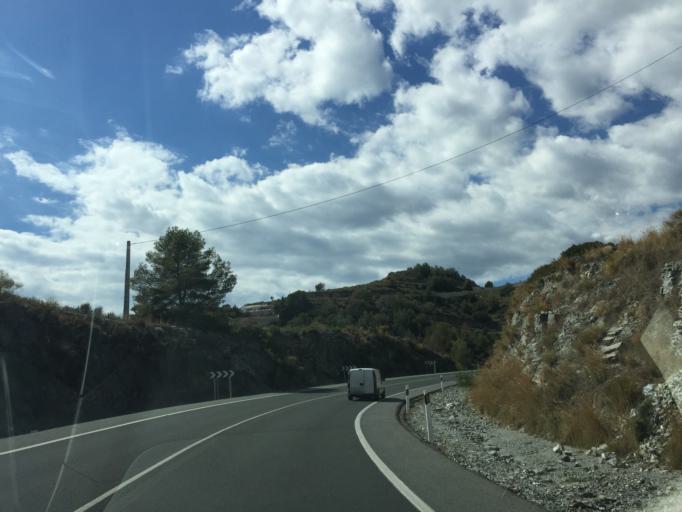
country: ES
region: Andalusia
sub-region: Provincia de Granada
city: La Herradura
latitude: 36.7367
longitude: -3.7189
